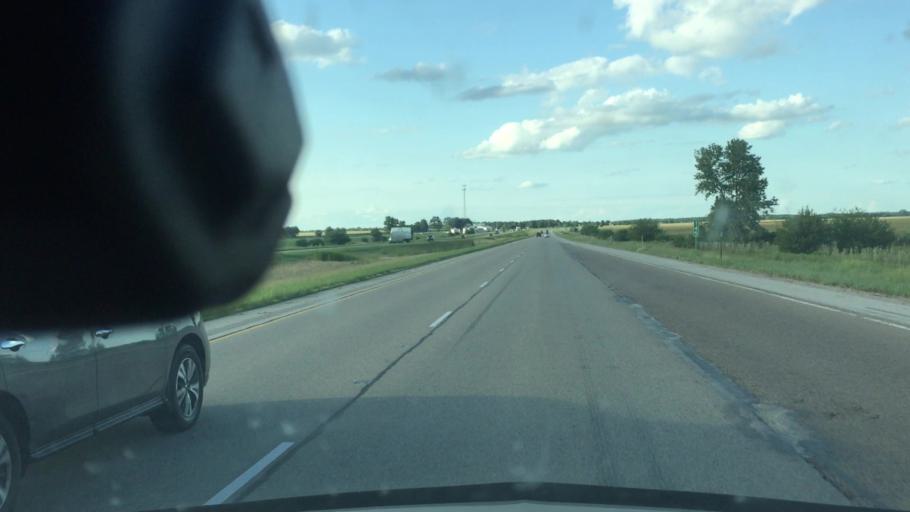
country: US
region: Illinois
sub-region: Logan County
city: Atlanta
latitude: 40.3156
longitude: -89.1598
